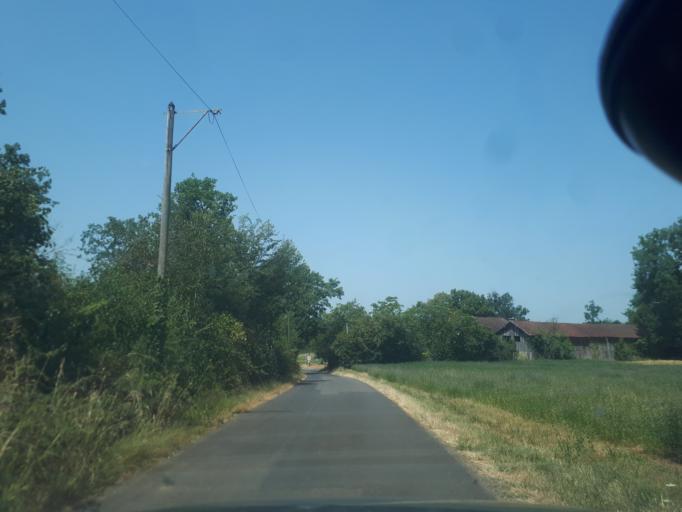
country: FR
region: Midi-Pyrenees
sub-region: Departement du Lot
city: Salviac
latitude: 44.7356
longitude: 1.2964
